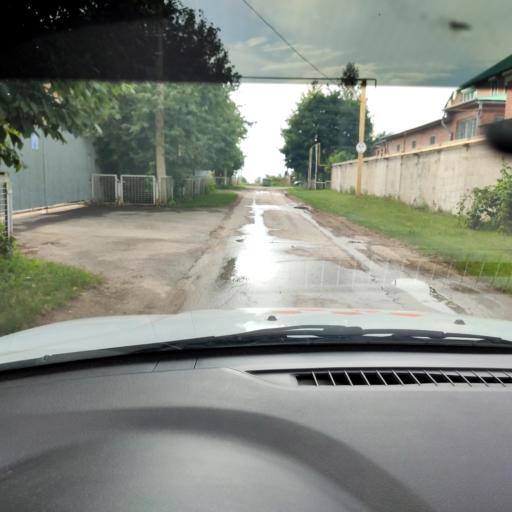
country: RU
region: Samara
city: Podstepki
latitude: 53.6102
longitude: 49.0322
